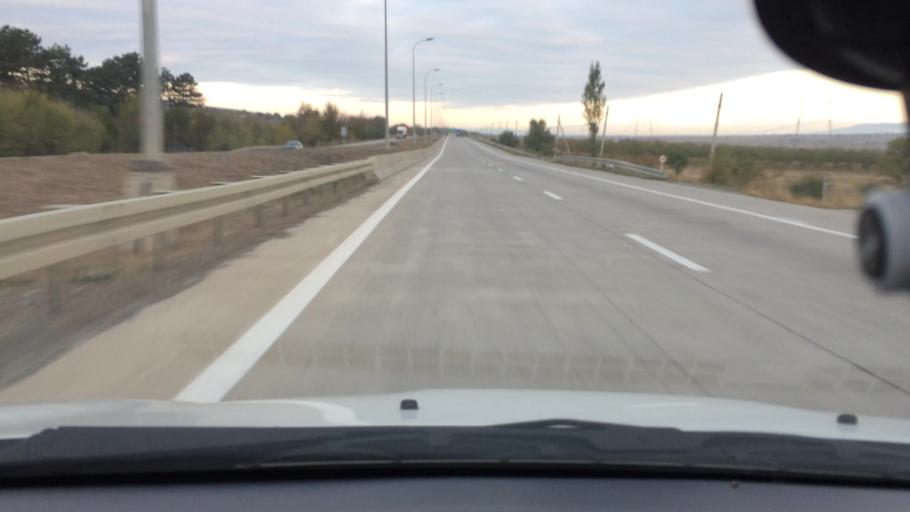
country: GE
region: Shida Kartli
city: Kaspi
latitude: 42.0085
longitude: 44.3442
